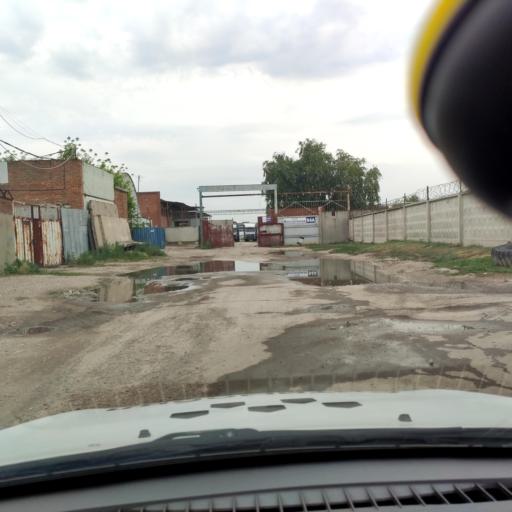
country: RU
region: Samara
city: Tol'yatti
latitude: 53.5759
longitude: 49.2653
